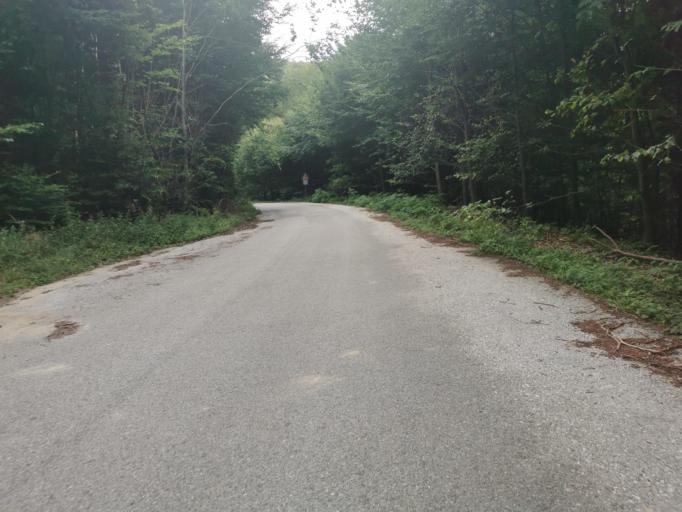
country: SK
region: Trenciansky
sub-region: Okres Myjava
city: Myjava
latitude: 48.8434
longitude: 17.6135
